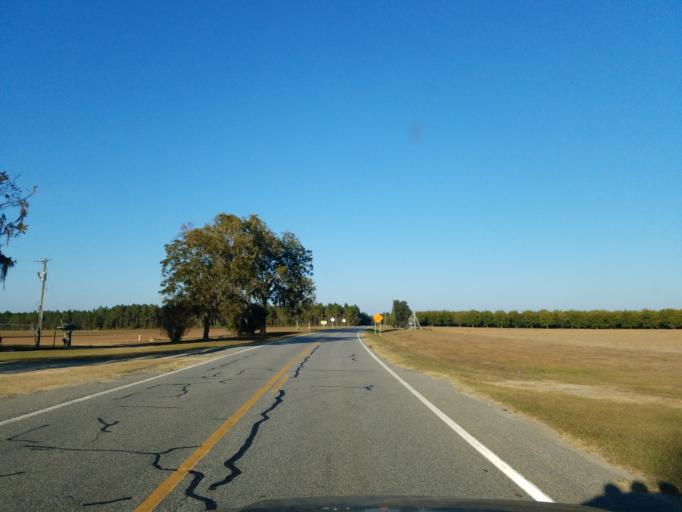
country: US
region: Georgia
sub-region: Lanier County
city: Lakeland
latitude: 30.9739
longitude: -83.0807
